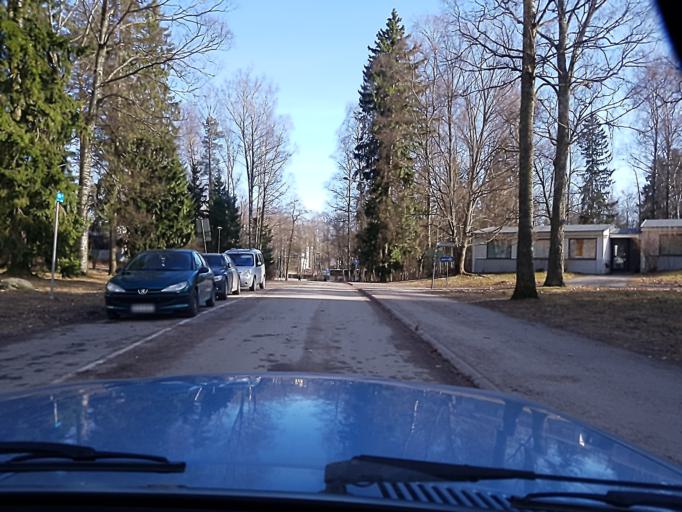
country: FI
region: Uusimaa
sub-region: Helsinki
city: Koukkuniemi
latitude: 60.1747
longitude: 24.7871
